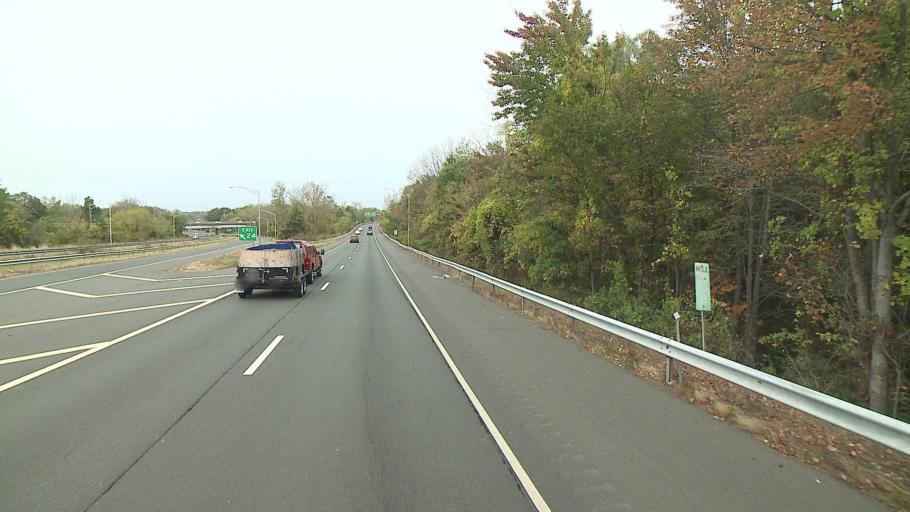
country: US
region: Connecticut
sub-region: Hartford County
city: Kensington
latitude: 41.6464
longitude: -72.7624
